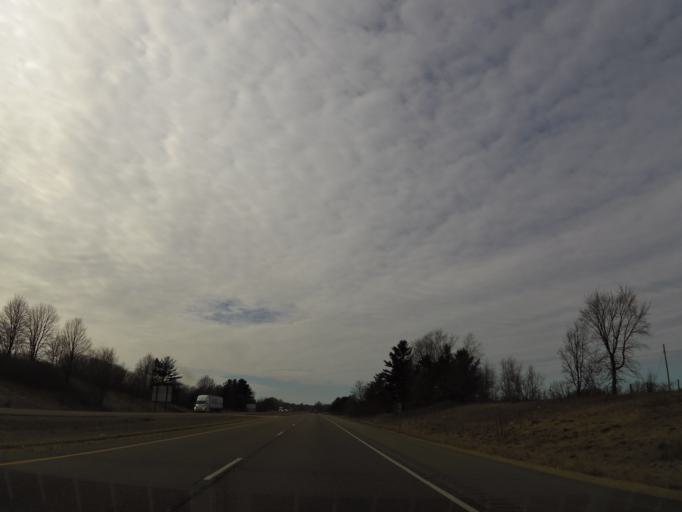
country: US
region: Wisconsin
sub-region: Dunn County
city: Menomonie
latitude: 44.9109
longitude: -91.9700
